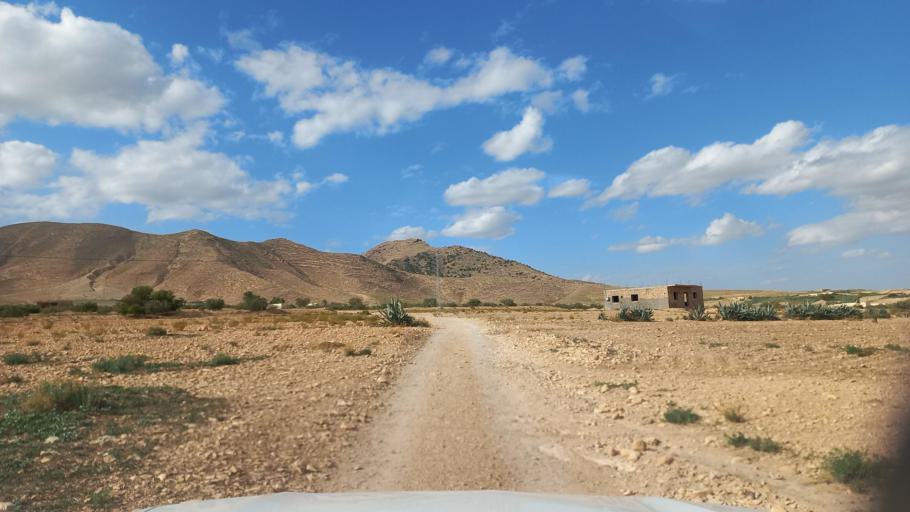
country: TN
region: Al Qasrayn
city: Sbiba
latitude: 35.4491
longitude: 9.0757
